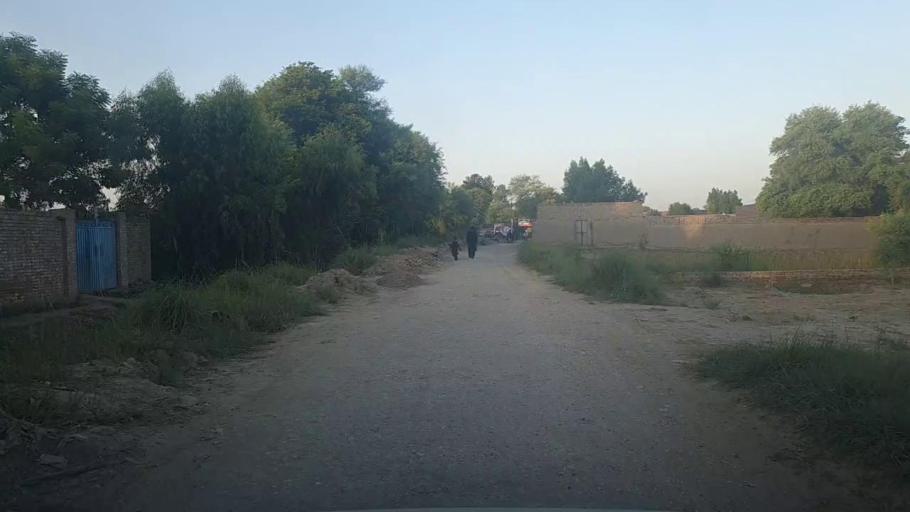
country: PK
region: Sindh
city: Khairpur
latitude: 28.0792
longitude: 69.7120
